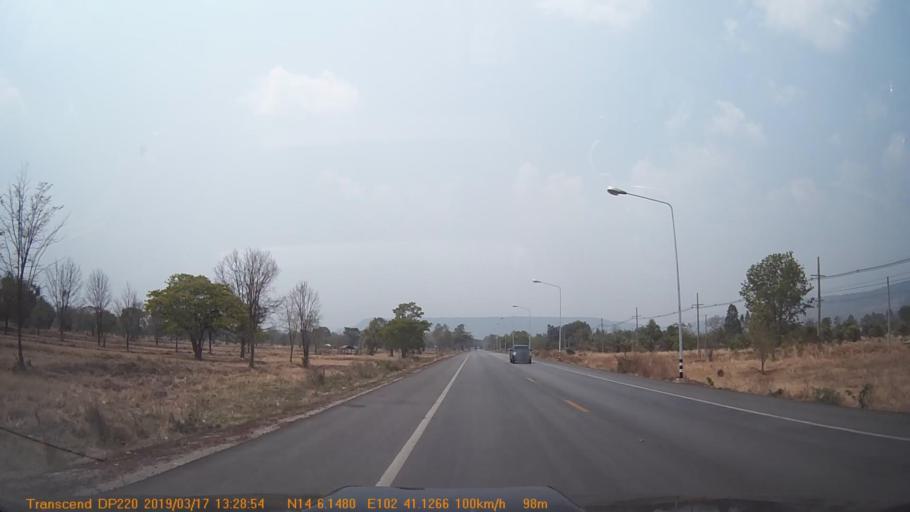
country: TH
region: Sa Kaeo
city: Ta Phraya
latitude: 14.1027
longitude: 102.6852
